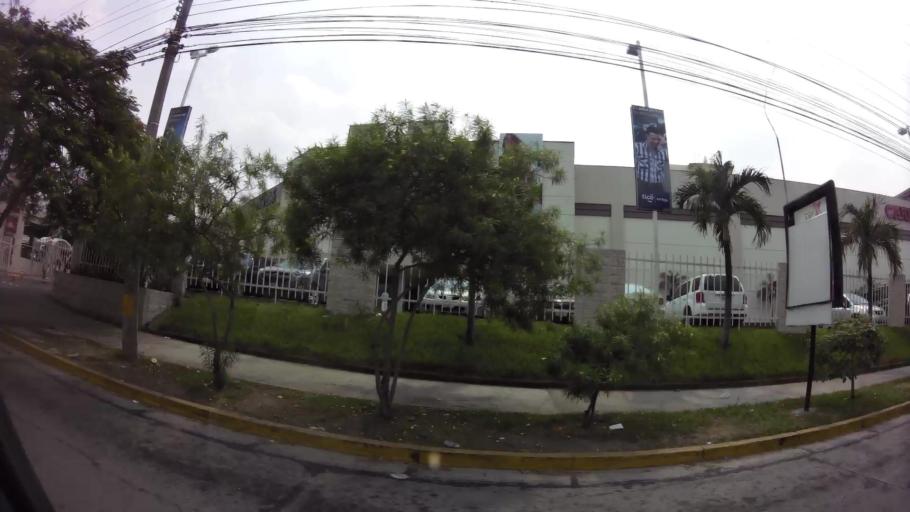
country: HN
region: Cortes
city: San Pedro Sula
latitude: 15.4944
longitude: -88.0336
